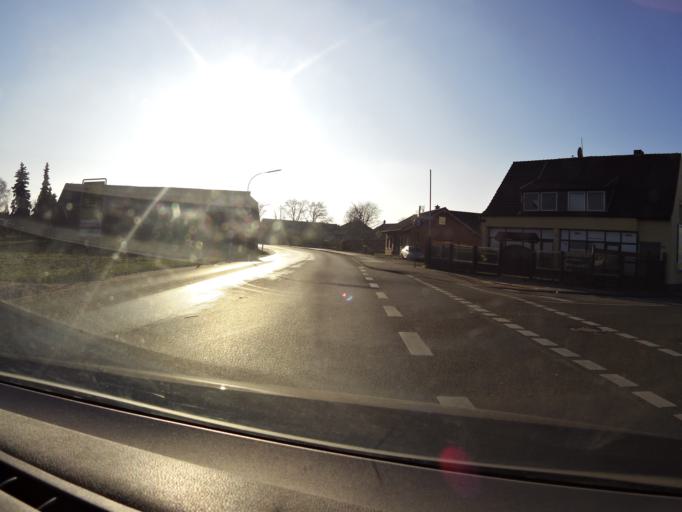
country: DE
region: North Rhine-Westphalia
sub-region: Regierungsbezirk Dusseldorf
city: Bruggen
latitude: 51.2573
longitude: 6.1846
